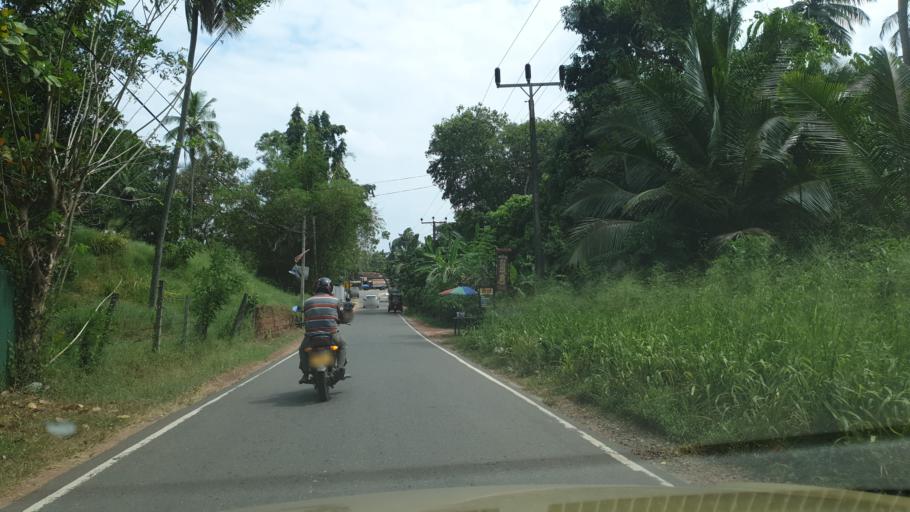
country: LK
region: North Western
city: Kuliyapitiya
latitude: 7.3476
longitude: 79.9830
